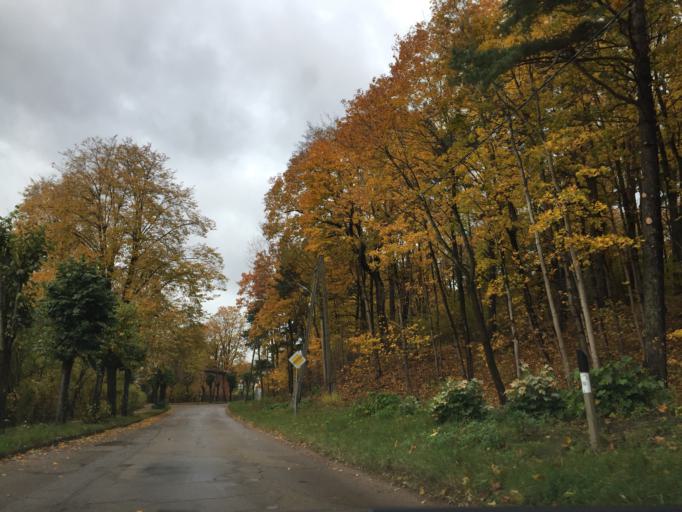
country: LV
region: Ogre
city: Ogre
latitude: 56.8121
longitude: 24.6151
